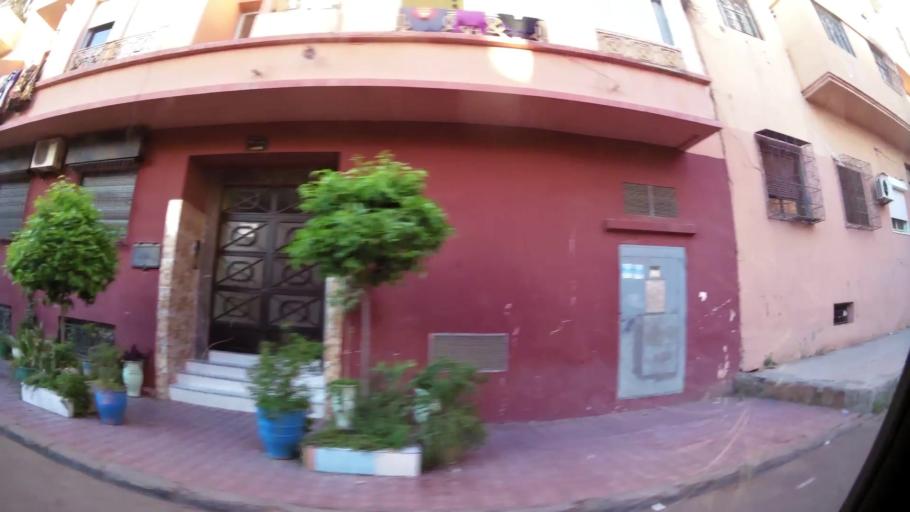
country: MA
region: Marrakech-Tensift-Al Haouz
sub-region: Marrakech
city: Marrakesh
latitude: 31.6215
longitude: -8.0284
